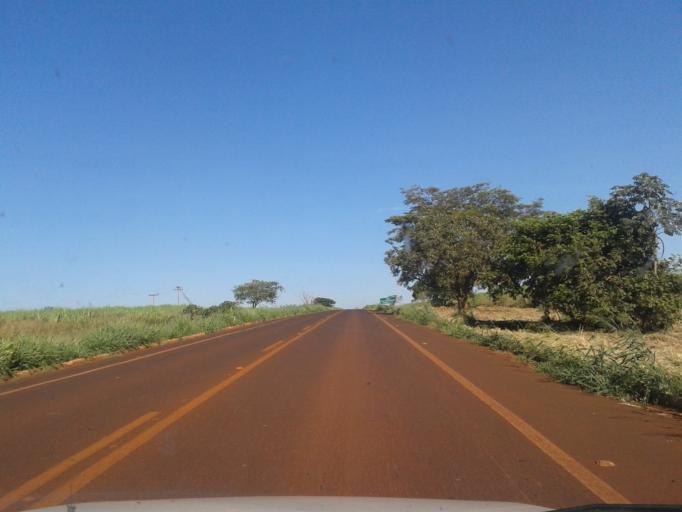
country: BR
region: Minas Gerais
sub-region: Capinopolis
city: Capinopolis
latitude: -18.7036
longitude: -49.6758
